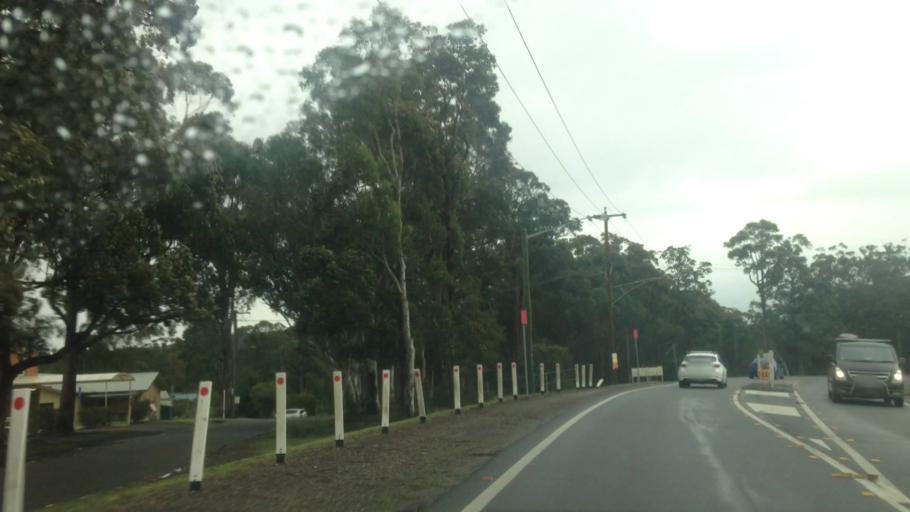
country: AU
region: New South Wales
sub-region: Wyong Shire
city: Charmhaven
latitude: -33.1686
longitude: 151.4760
